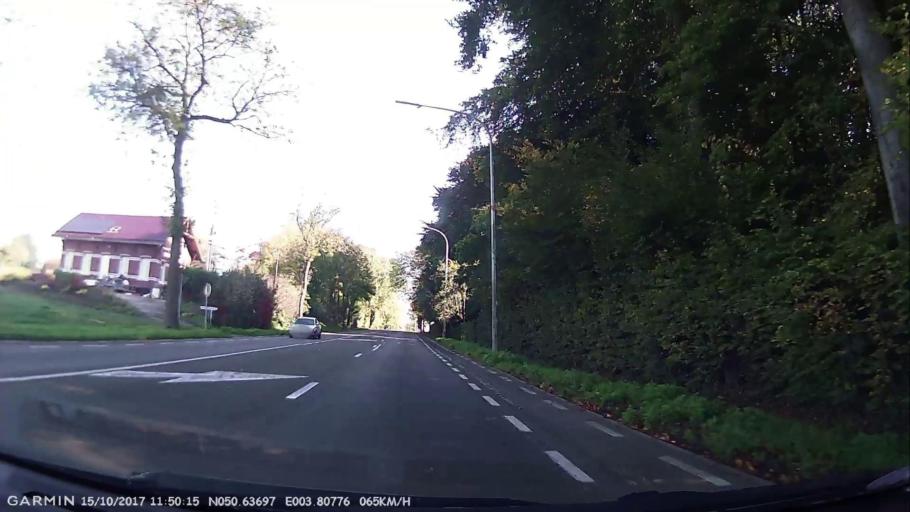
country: BE
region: Wallonia
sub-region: Province du Hainaut
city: Ath
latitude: 50.6370
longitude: 3.8080
